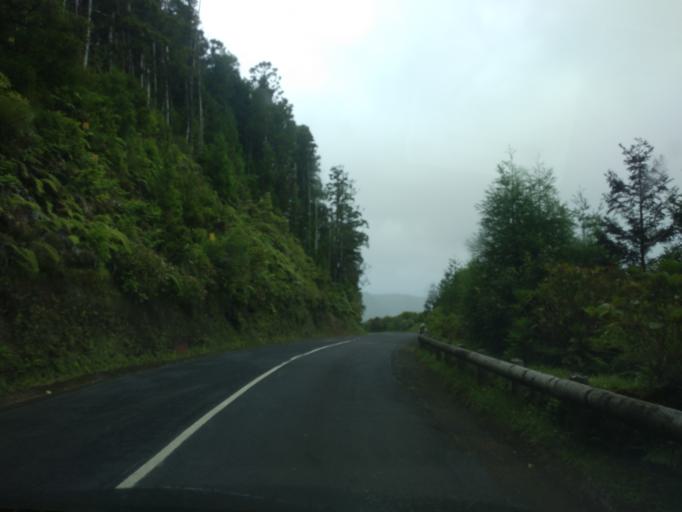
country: PT
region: Azores
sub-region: Ponta Delgada
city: Arrifes
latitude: 37.8375
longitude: -25.7863
